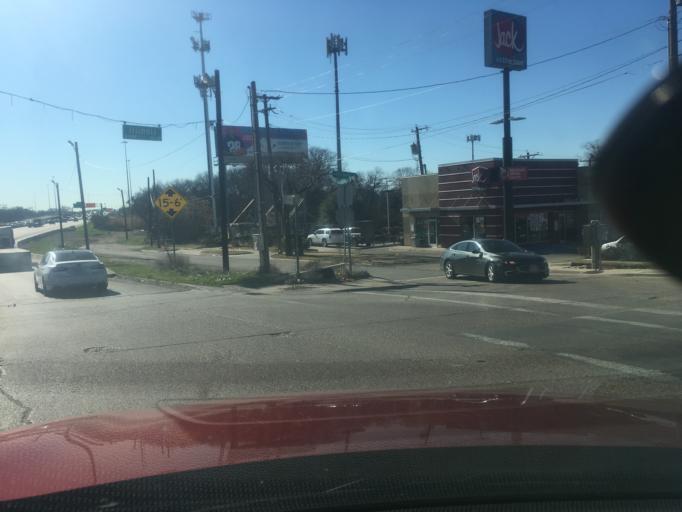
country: US
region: Texas
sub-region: Dallas County
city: Cockrell Hill
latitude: 32.7204
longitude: -96.8281
